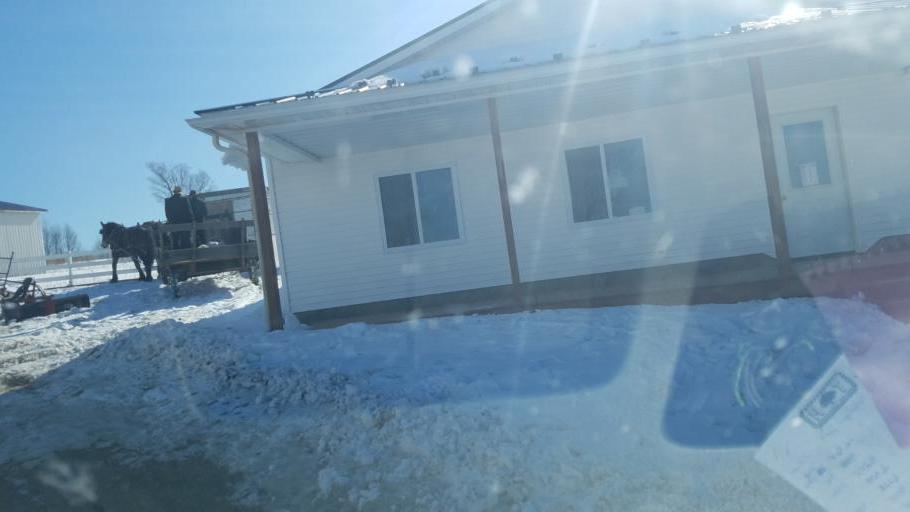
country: US
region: Pennsylvania
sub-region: Tioga County
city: Westfield
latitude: 41.9240
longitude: -77.7564
